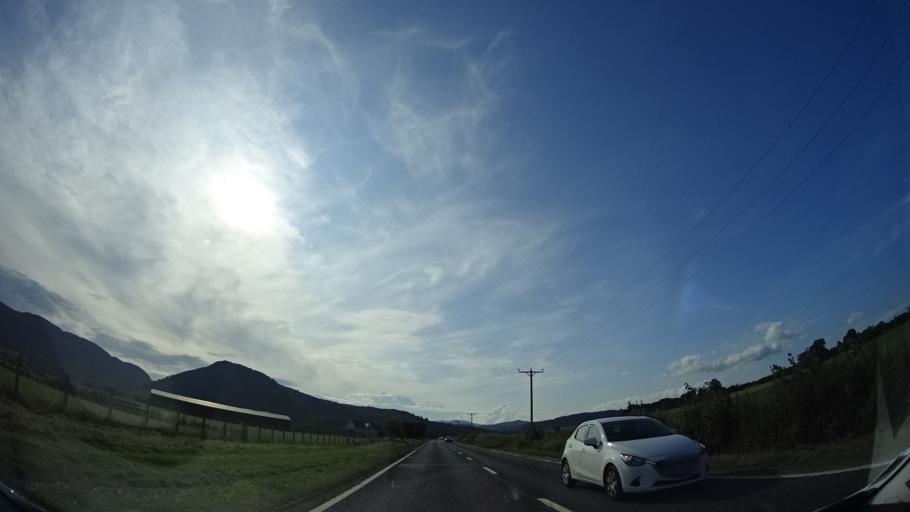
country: GB
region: Scotland
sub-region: Highland
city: Muir of Ord
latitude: 57.5618
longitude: -4.5669
